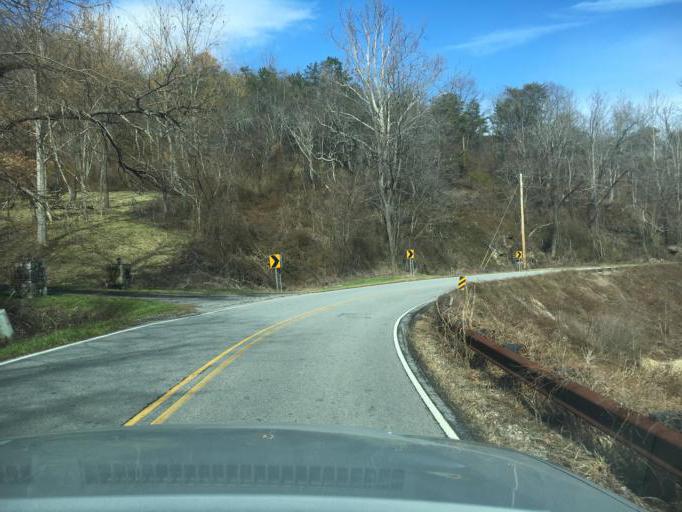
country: US
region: North Carolina
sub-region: Haywood County
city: Clyde
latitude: 35.4948
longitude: -82.8841
